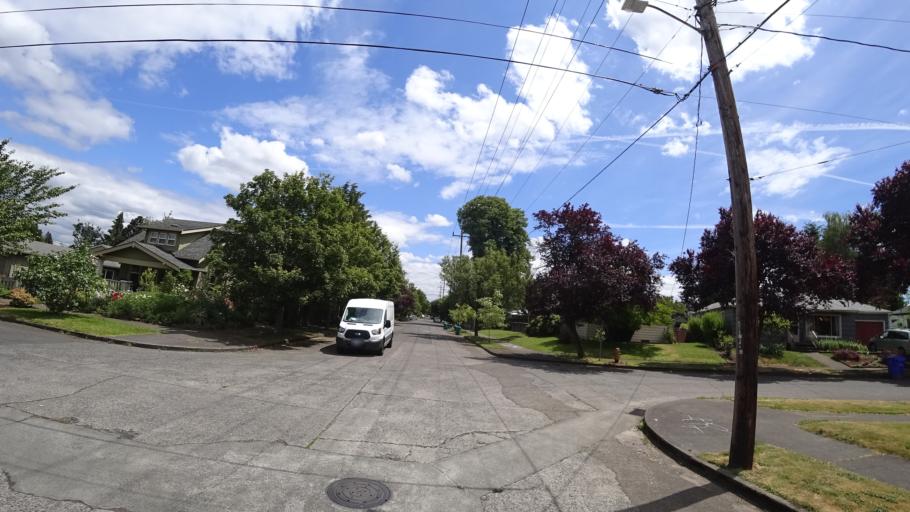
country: US
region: Oregon
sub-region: Multnomah County
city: Portland
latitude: 45.5865
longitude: -122.7233
